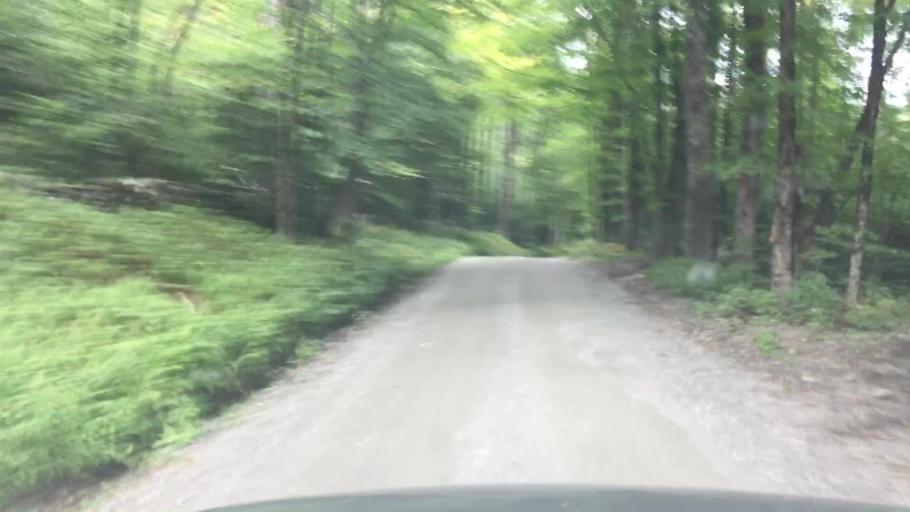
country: US
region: Vermont
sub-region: Windham County
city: Dover
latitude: 42.8409
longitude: -72.7675
